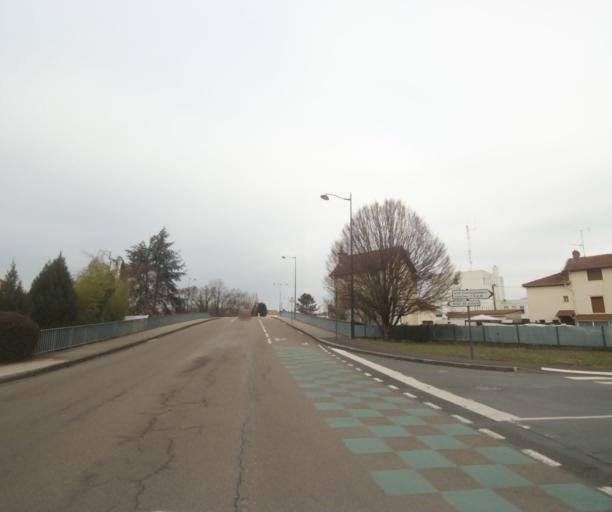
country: FR
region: Champagne-Ardenne
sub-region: Departement de la Haute-Marne
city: Bettancourt-la-Ferree
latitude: 48.6388
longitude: 4.9624
